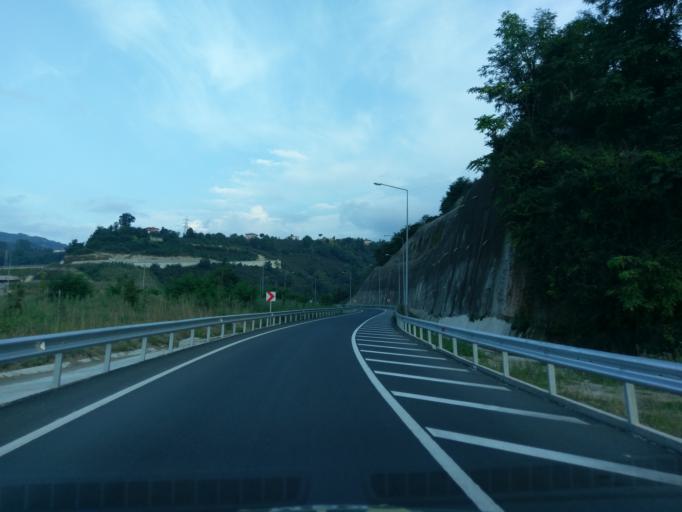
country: TR
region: Ordu
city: Ordu
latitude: 40.9887
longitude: 37.8086
